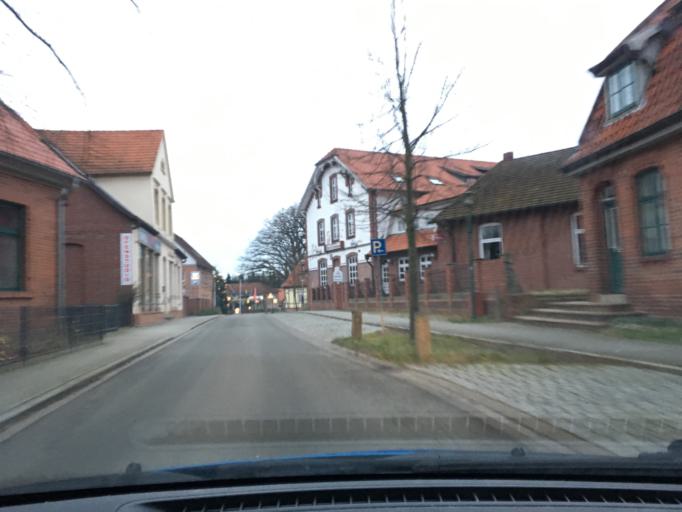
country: DE
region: Lower Saxony
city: Neu Darchau
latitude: 53.2848
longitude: 10.9295
